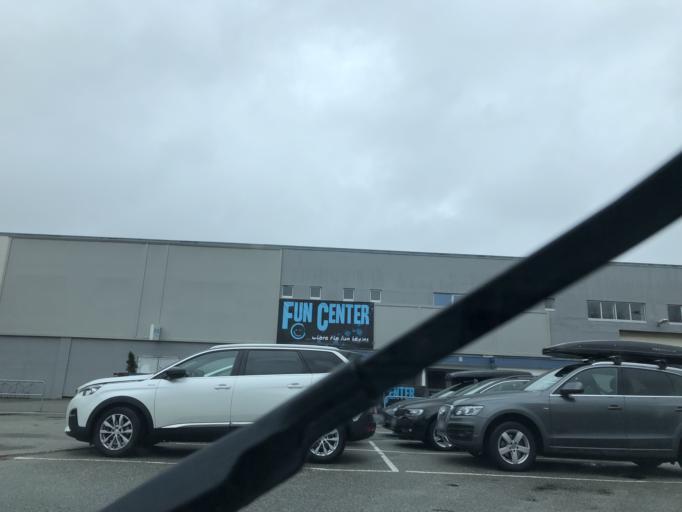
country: NO
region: Rogaland
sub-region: Sandnes
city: Sandnes
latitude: 58.8493
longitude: 5.7405
